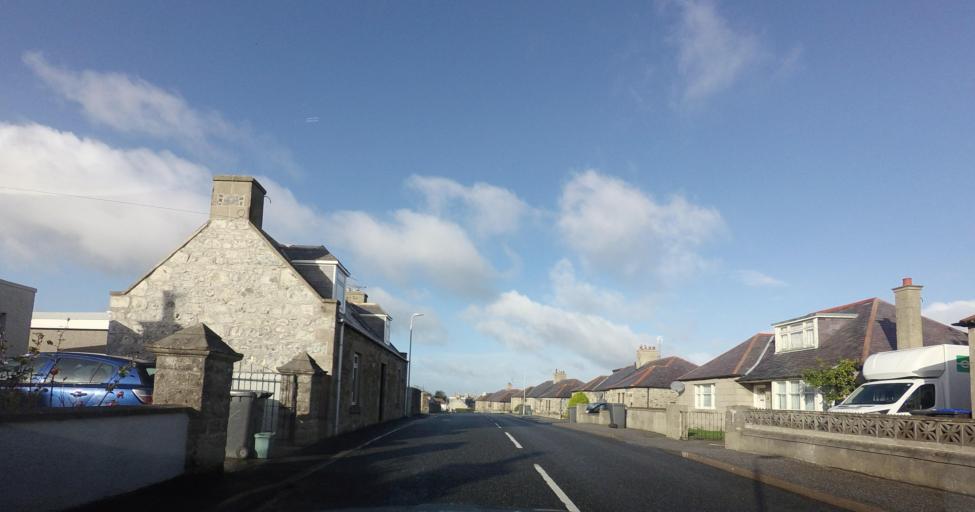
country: GB
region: Scotland
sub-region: Aberdeenshire
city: Whitehills
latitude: 57.6763
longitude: -2.5762
